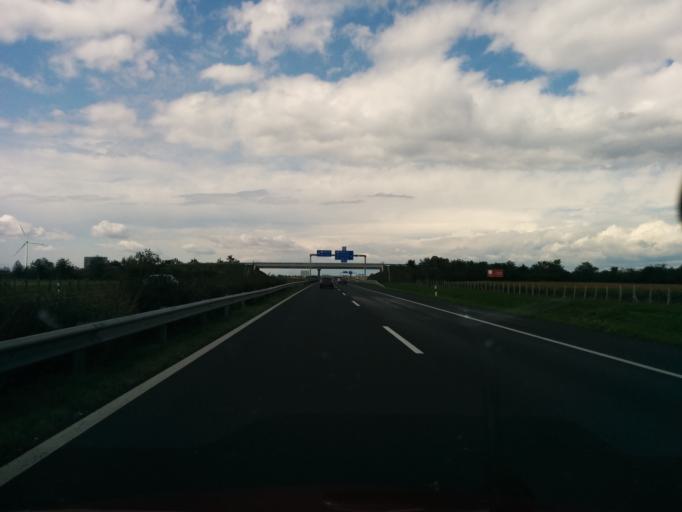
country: HU
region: Gyor-Moson-Sopron
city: Mosonmagyarovar
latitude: 47.8821
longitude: 17.1956
